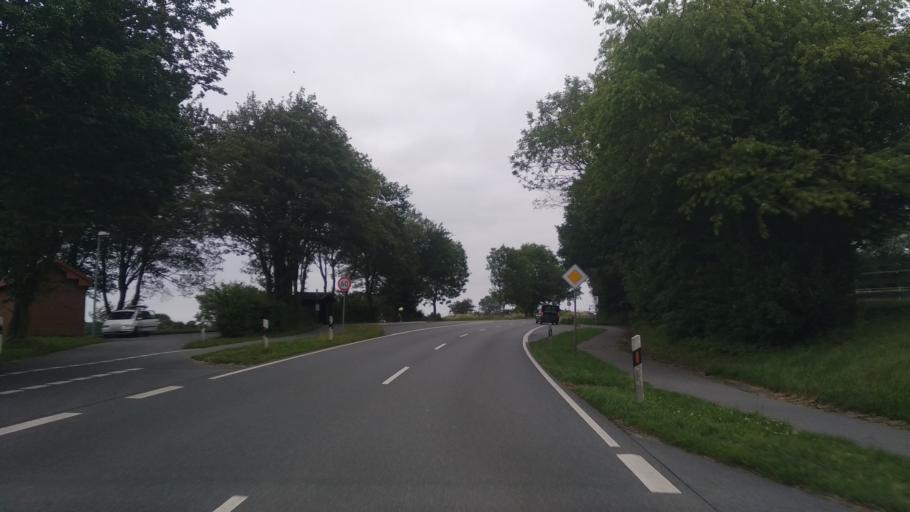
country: DE
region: Schleswig-Holstein
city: Munkbrarup
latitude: 54.8070
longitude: 9.5664
